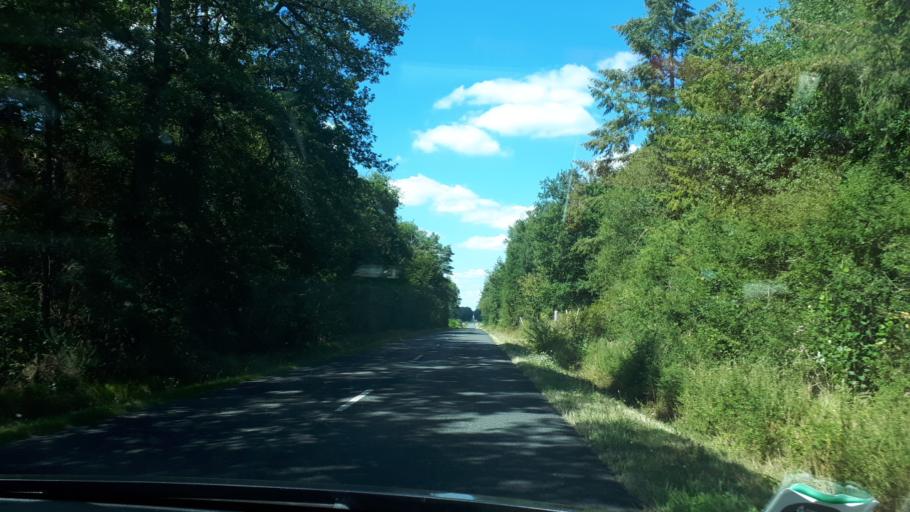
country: FR
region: Centre
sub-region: Departement du Loir-et-Cher
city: Neung-sur-Beuvron
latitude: 47.5340
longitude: 1.7394
